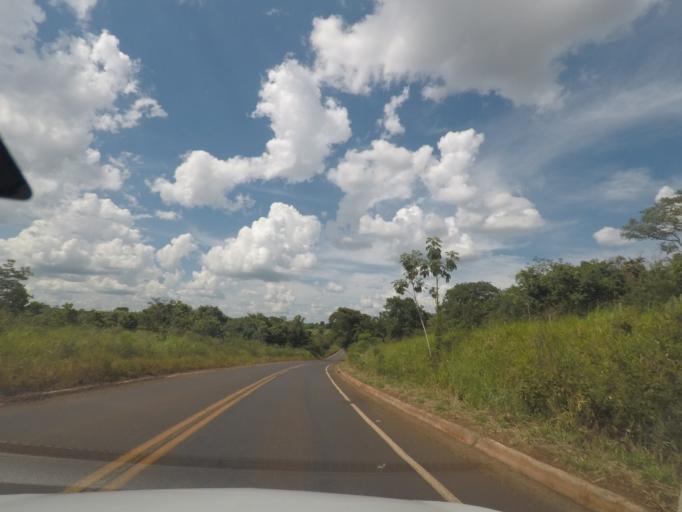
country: BR
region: Minas Gerais
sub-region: Conceicao Das Alagoas
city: Conceicao das Alagoas
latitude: -19.8183
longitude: -48.5905
